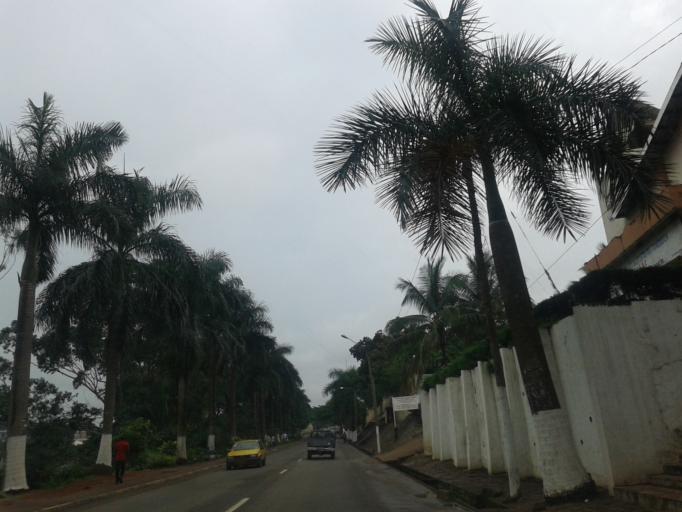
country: CM
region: Centre
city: Yaounde
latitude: 3.8762
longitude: 11.5141
